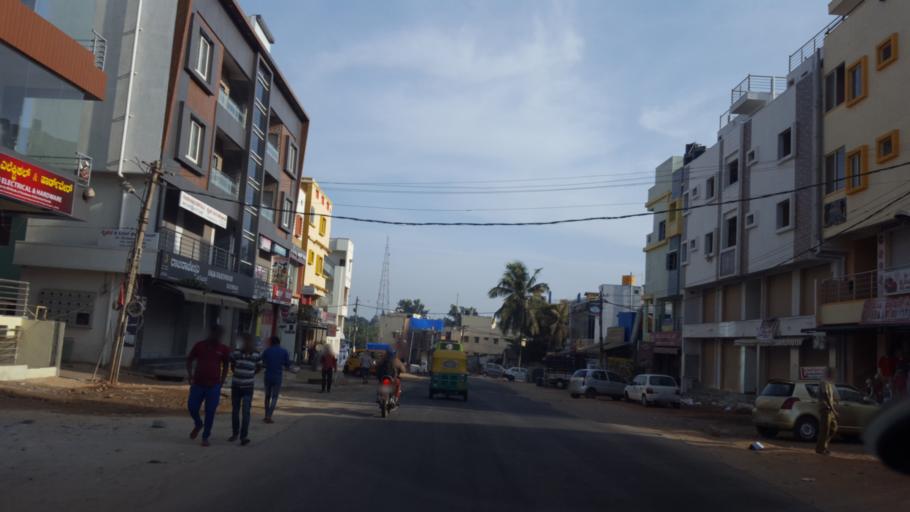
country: IN
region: Karnataka
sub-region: Bangalore Urban
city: Bangalore
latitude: 12.9214
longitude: 77.5144
